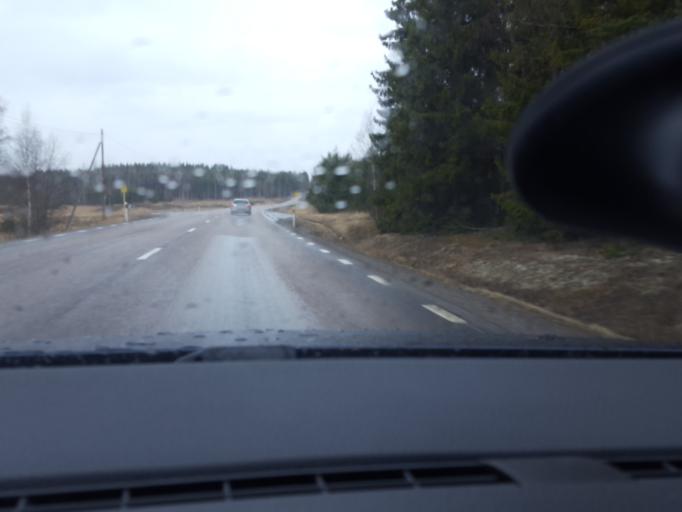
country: SE
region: Vaermland
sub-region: Sunne Kommun
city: Sunne
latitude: 59.6333
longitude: 12.9480
